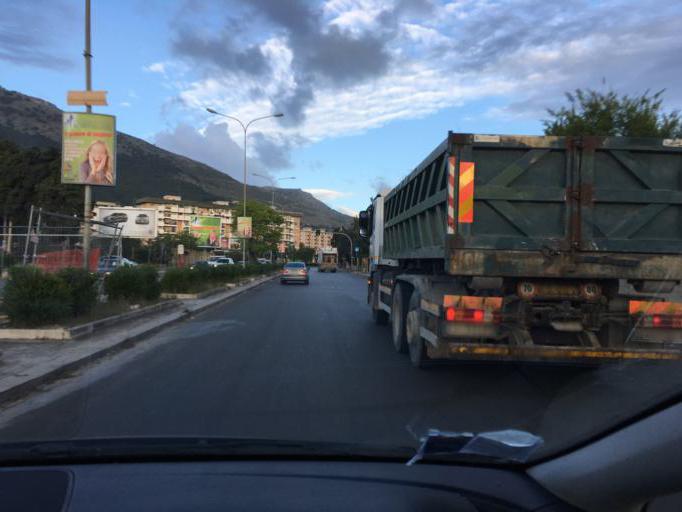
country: IT
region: Sicily
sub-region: Palermo
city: Isola delle Femmine
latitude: 38.1890
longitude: 13.2980
